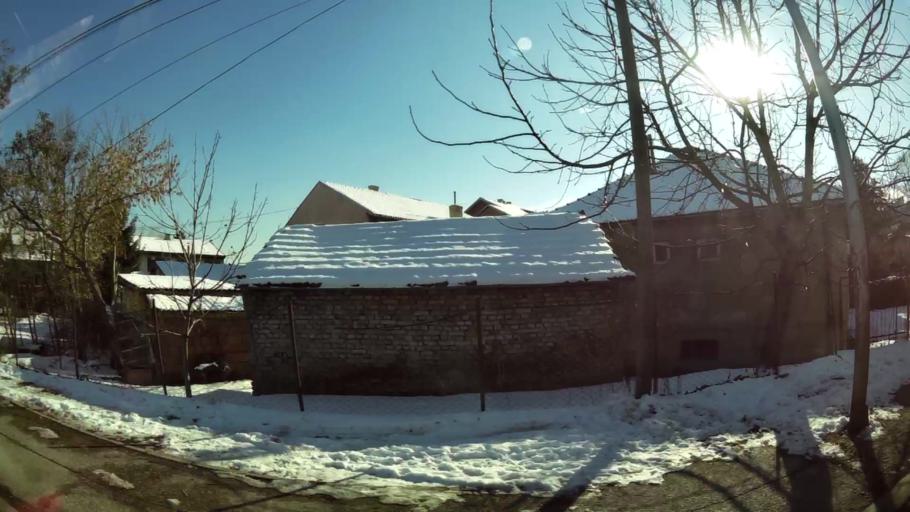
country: MK
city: Krushopek
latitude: 42.0099
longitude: 21.3722
